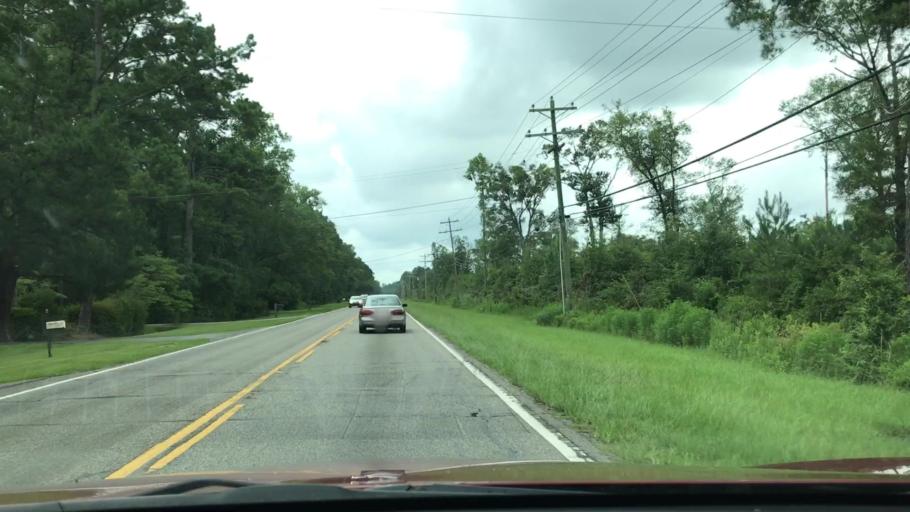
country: US
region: South Carolina
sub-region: Georgetown County
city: Georgetown
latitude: 33.4299
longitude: -79.2789
